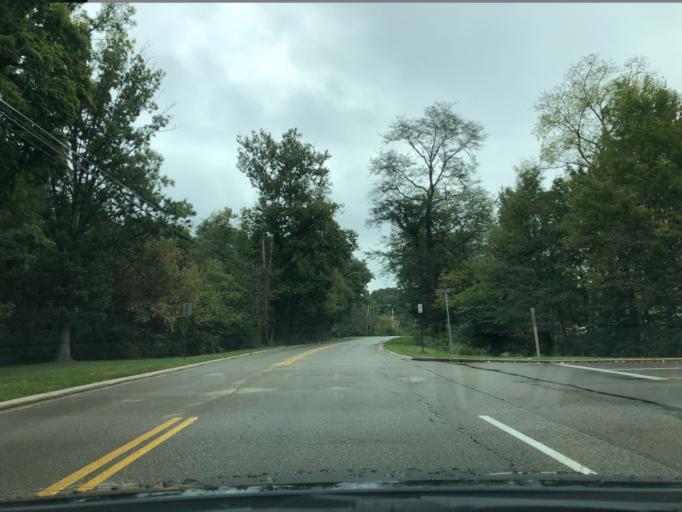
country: US
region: Ohio
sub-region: Hamilton County
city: Sharonville
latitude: 39.2852
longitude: -84.3916
